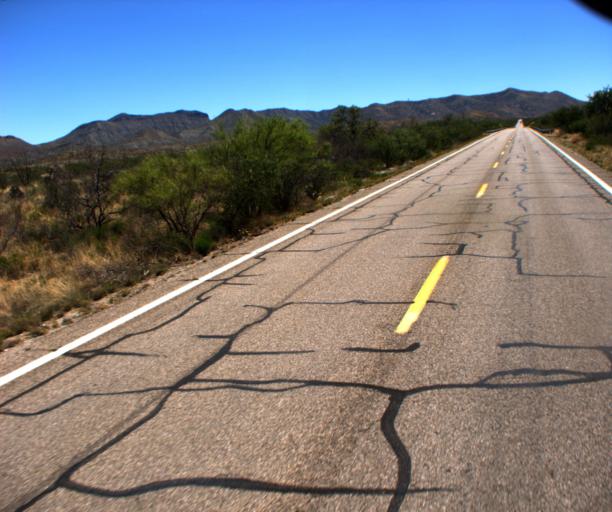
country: US
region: Arizona
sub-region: Pima County
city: Vail
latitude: 31.9491
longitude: -110.6663
